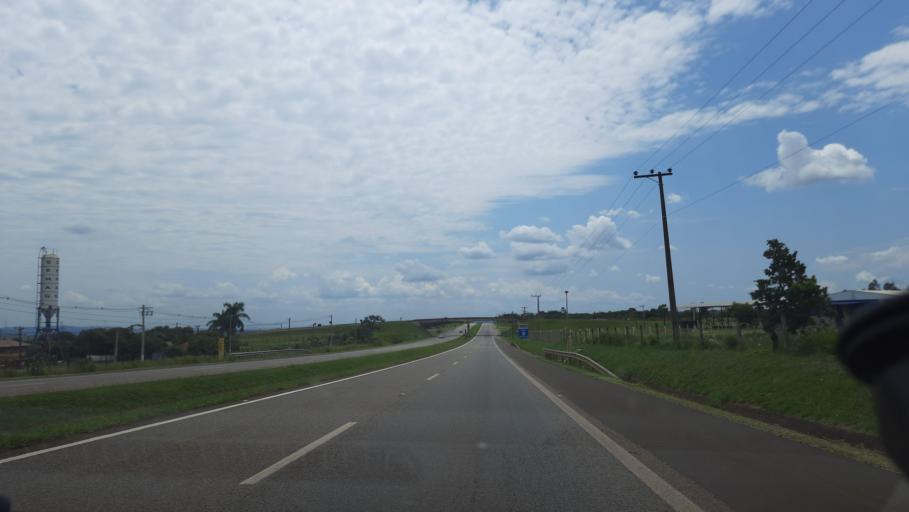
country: BR
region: Sao Paulo
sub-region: Casa Branca
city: Casa Branca
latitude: -21.7516
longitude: -47.0714
